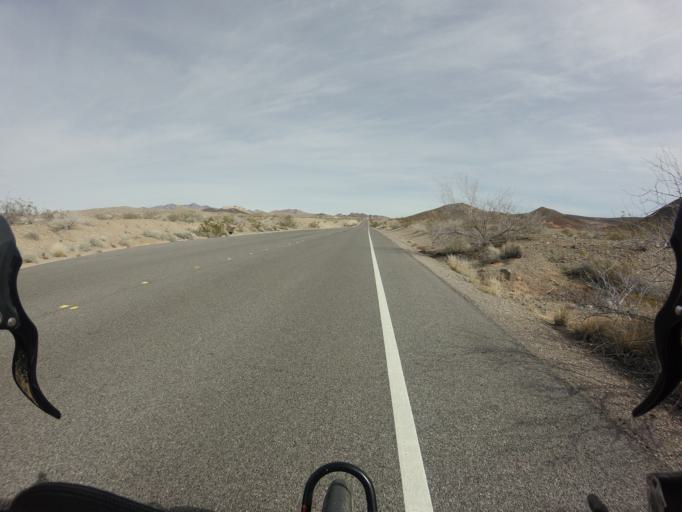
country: US
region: Nevada
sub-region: Clark County
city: Boulder City
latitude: 36.1734
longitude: -114.7761
